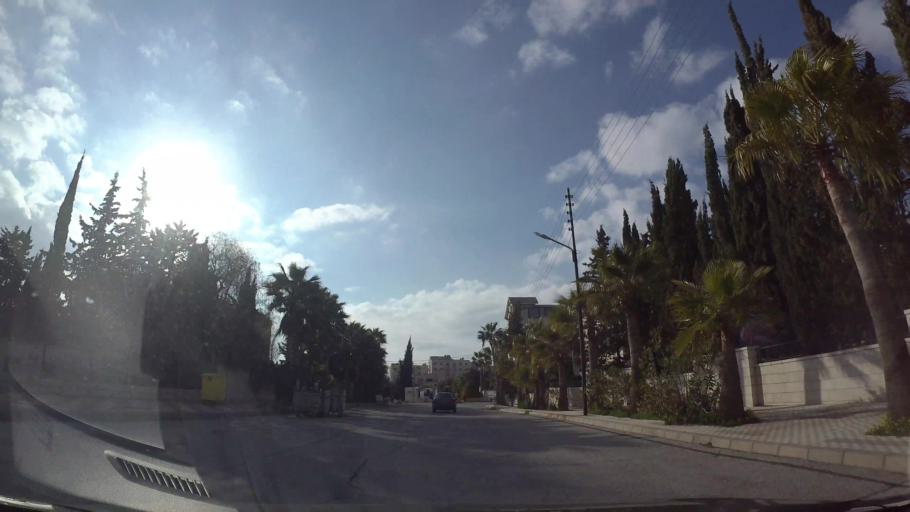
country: JO
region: Amman
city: Al Jubayhah
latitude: 31.9829
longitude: 35.8800
